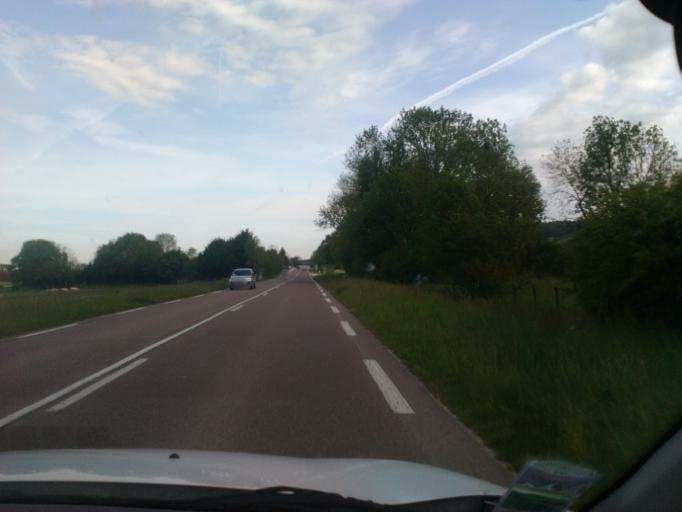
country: FR
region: Champagne-Ardenne
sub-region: Departement de l'Aube
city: Bar-sur-Aube
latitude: 48.2502
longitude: 4.6873
